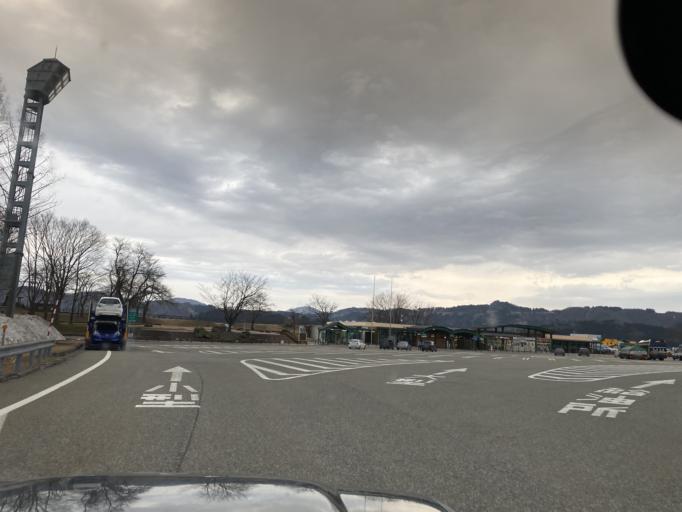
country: JP
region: Niigata
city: Ojiya
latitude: 37.2710
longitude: 138.8367
